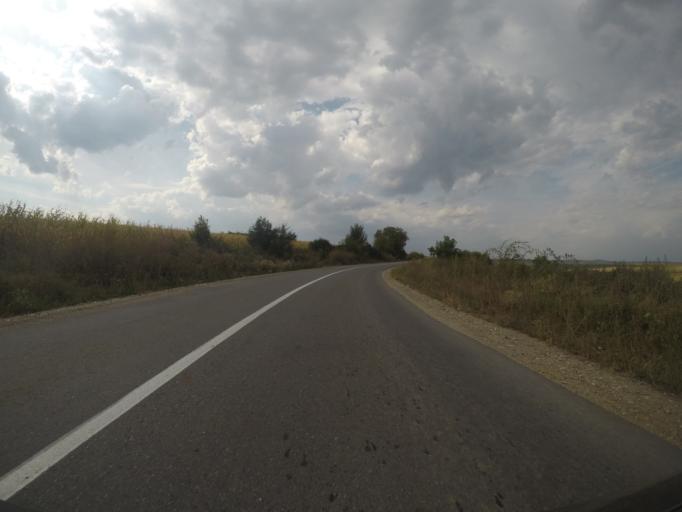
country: RO
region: Cluj
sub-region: Comuna Sandulesti
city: Copaceni
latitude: 46.5859
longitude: 23.7500
